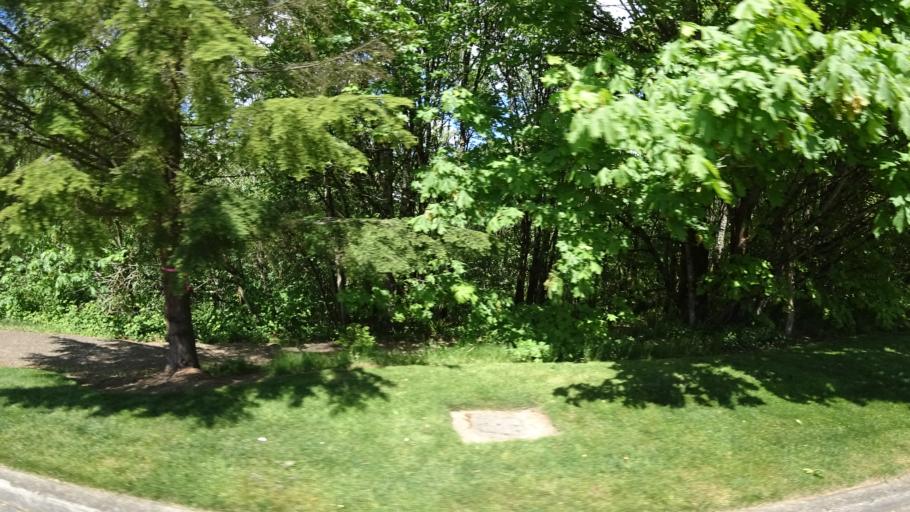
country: US
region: Oregon
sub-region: Washington County
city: West Haven
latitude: 45.5355
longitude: -122.7687
